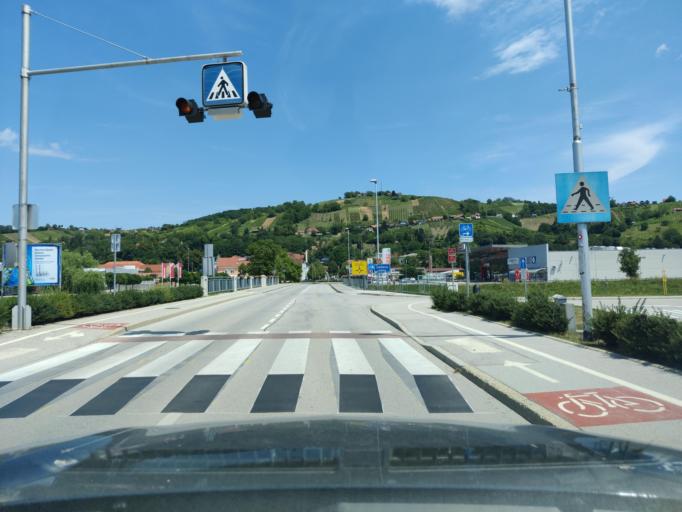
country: SI
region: Lendava-Lendva
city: Lendava
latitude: 46.5604
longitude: 16.4500
